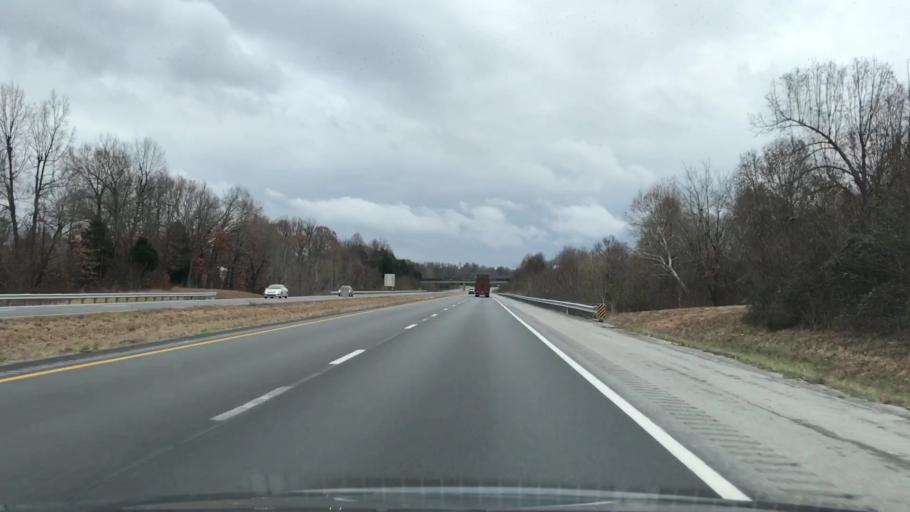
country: US
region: Kentucky
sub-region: Hopkins County
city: Madisonville
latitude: 37.3996
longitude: -87.4756
